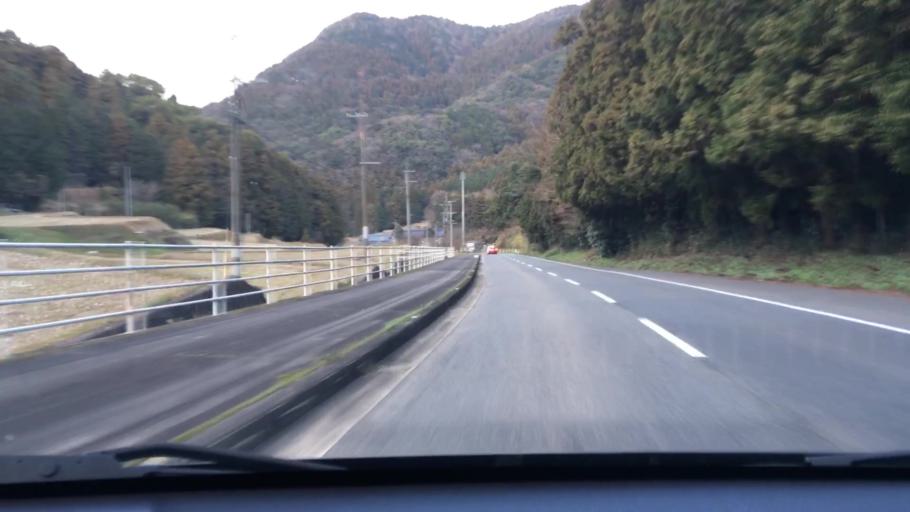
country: JP
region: Oita
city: Bungo-Takada-shi
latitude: 33.4788
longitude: 131.3861
